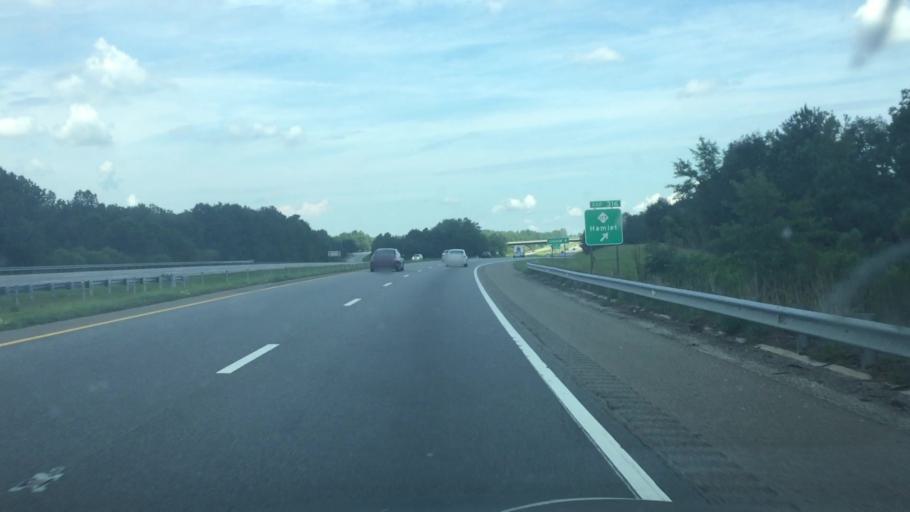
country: US
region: North Carolina
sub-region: Richmond County
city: Hamlet
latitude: 34.8544
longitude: -79.7378
